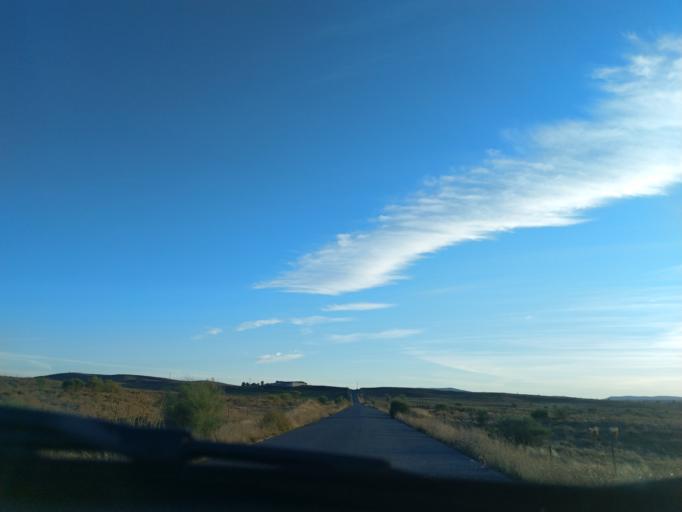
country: ES
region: Extremadura
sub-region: Provincia de Badajoz
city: Berlanga
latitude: 38.2675
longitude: -5.8235
